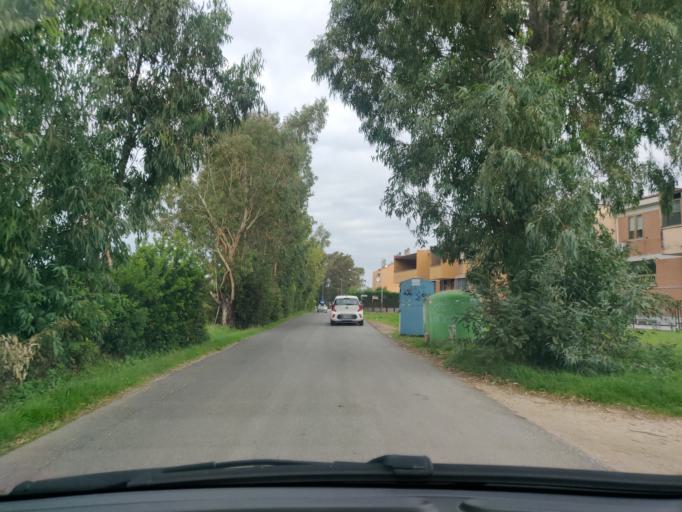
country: IT
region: Latium
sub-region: Citta metropolitana di Roma Capitale
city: Aurelia
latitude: 42.1365
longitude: 11.7828
